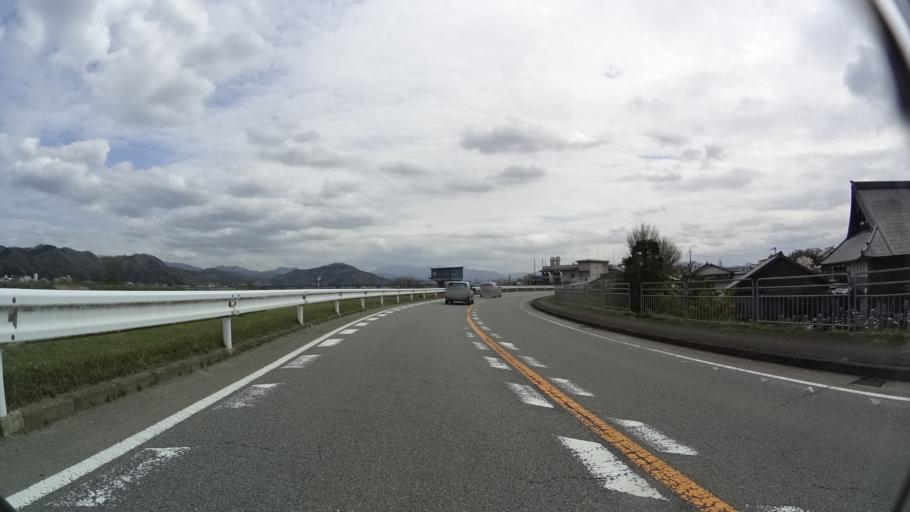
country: JP
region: Hyogo
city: Toyooka
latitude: 35.5482
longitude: 134.8262
